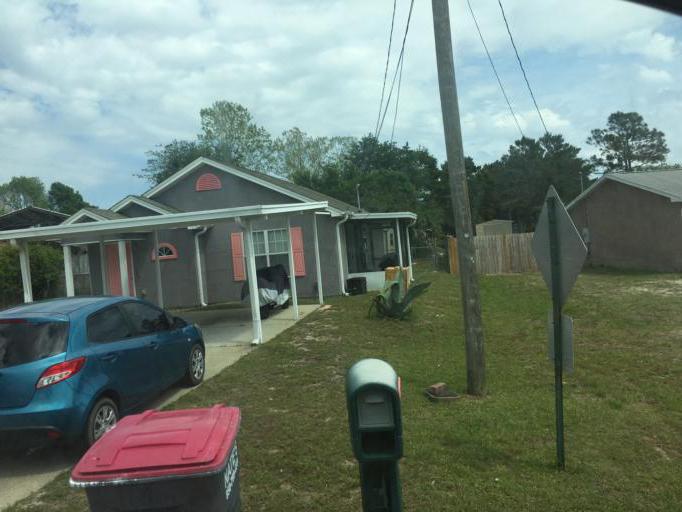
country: US
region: Florida
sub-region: Bay County
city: Laguna Beach
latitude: 30.2329
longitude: -85.8919
